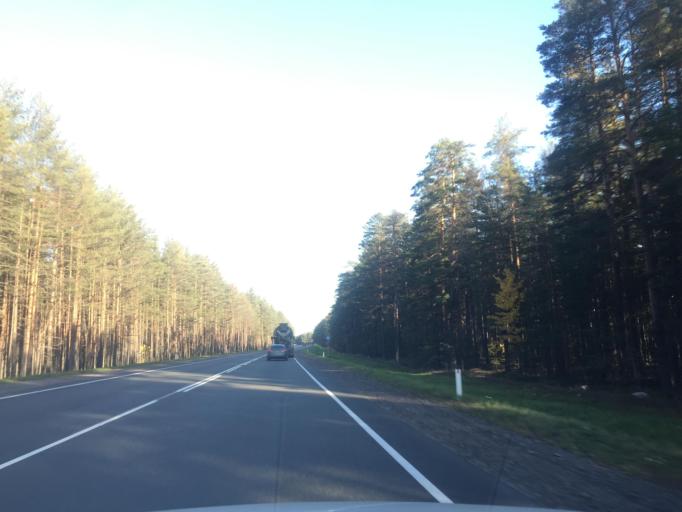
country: RU
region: Leningrad
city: Priozersk
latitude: 60.9858
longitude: 30.1835
